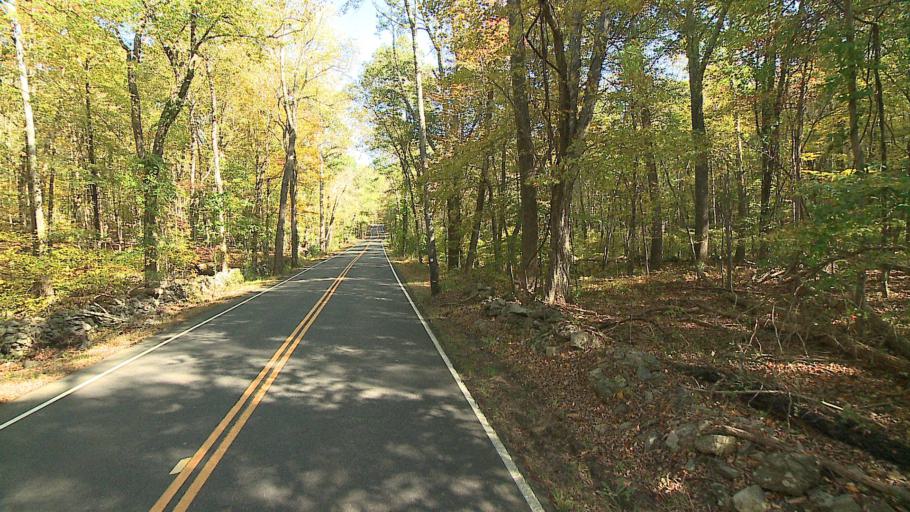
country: US
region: Connecticut
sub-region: Fairfield County
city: Southport
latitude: 41.2389
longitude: -73.3106
